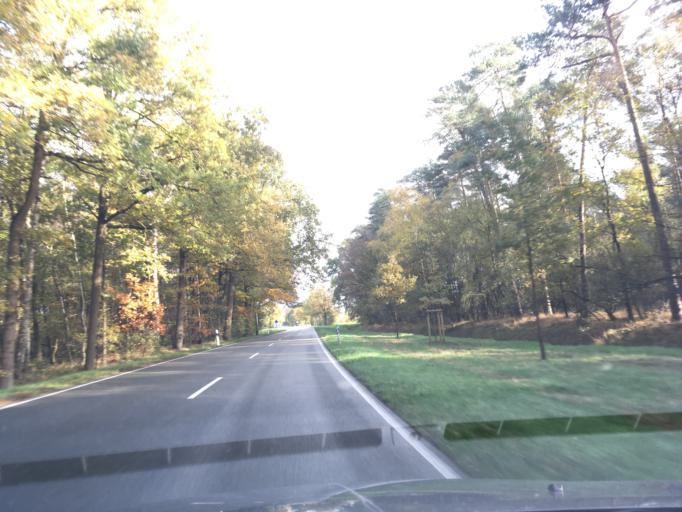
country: DE
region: North Rhine-Westphalia
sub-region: Regierungsbezirk Munster
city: Vreden
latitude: 52.0932
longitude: 6.8225
